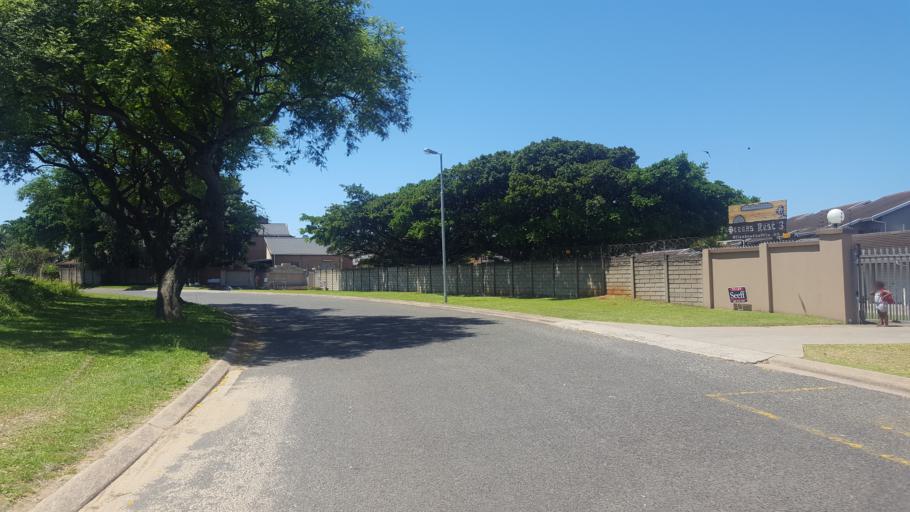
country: ZA
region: KwaZulu-Natal
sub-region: uThungulu District Municipality
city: Richards Bay
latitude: -28.7657
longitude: 32.0693
